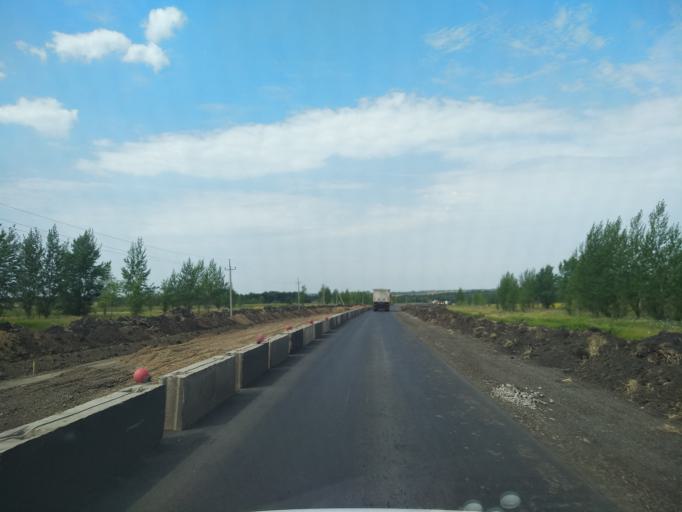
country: RU
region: Voronezj
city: Verkhnyaya Khava
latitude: 51.6751
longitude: 39.8350
